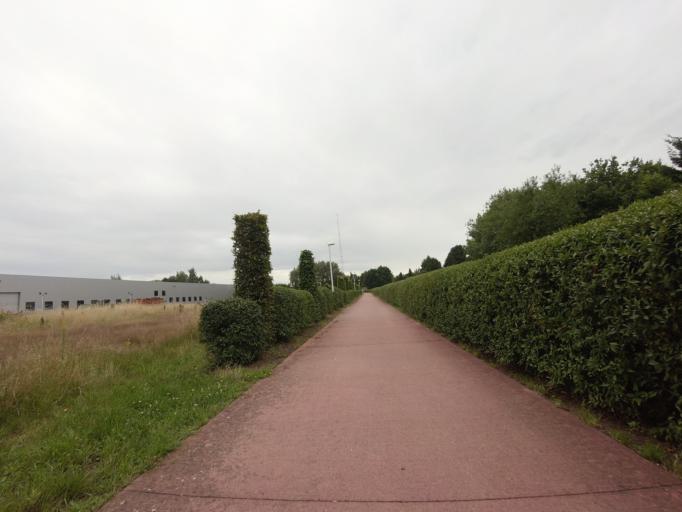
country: BE
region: Flanders
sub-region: Provincie Antwerpen
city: Lier
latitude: 51.1094
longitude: 4.5455
